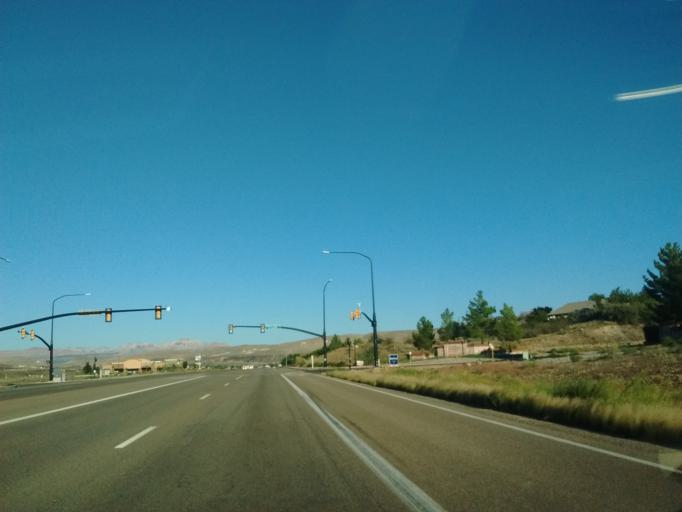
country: US
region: Utah
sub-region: Washington County
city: Hurricane
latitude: 37.1763
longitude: -113.3304
